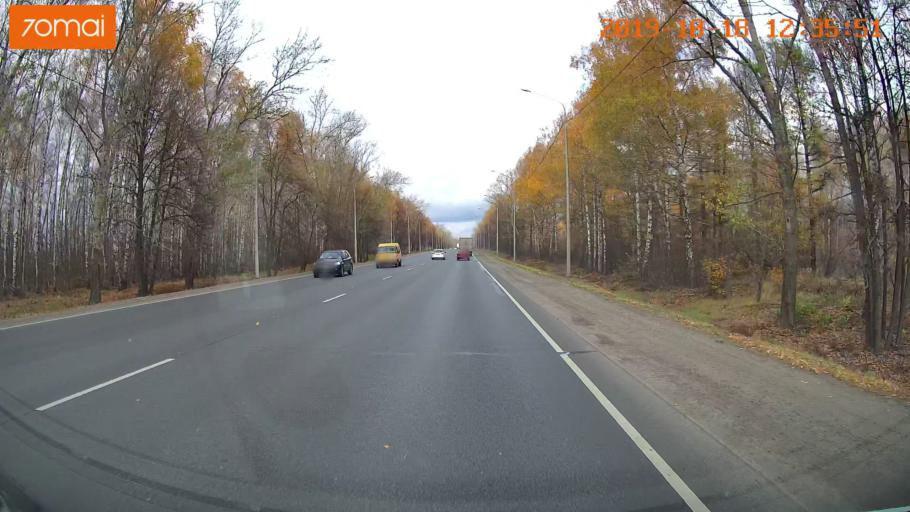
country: RU
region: Rjazan
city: Ryazan'
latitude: 54.6287
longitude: 39.6349
